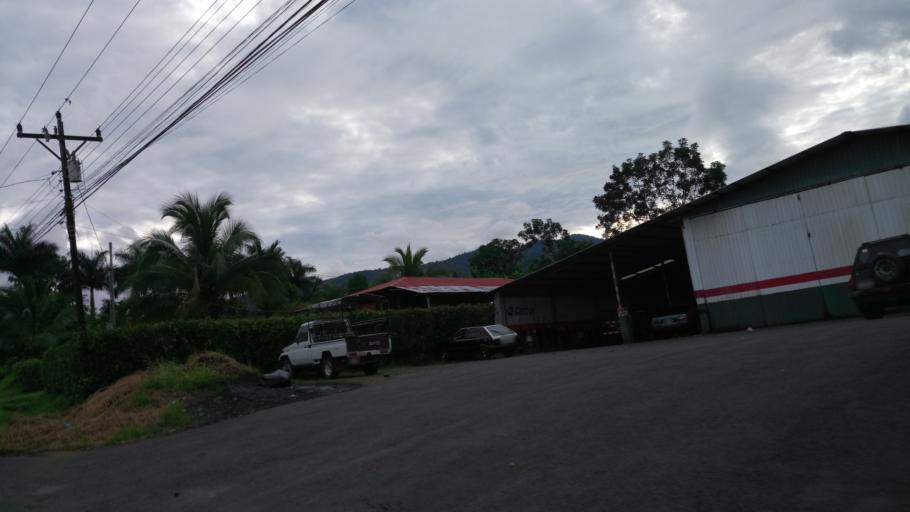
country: CR
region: Alajuela
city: Pocosol
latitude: 10.3567
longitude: -84.5895
